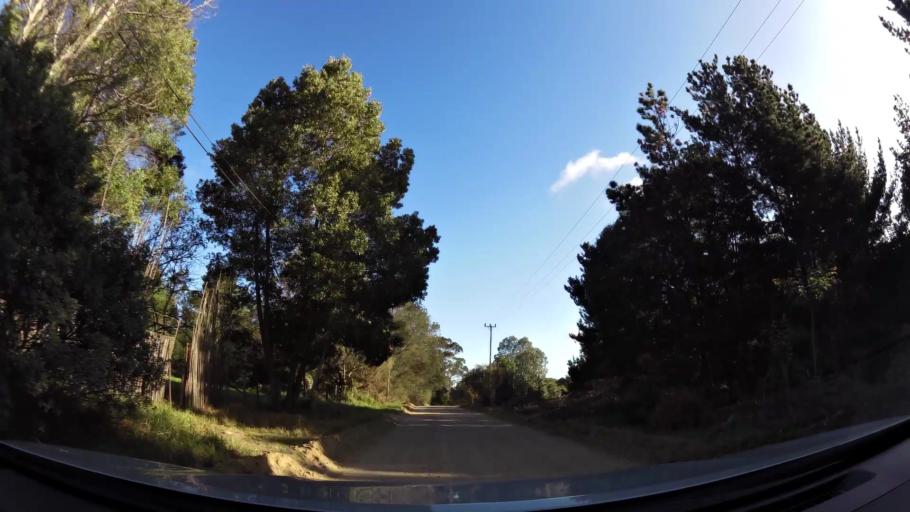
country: ZA
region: Western Cape
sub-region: Eden District Municipality
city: George
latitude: -33.9788
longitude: 22.5738
